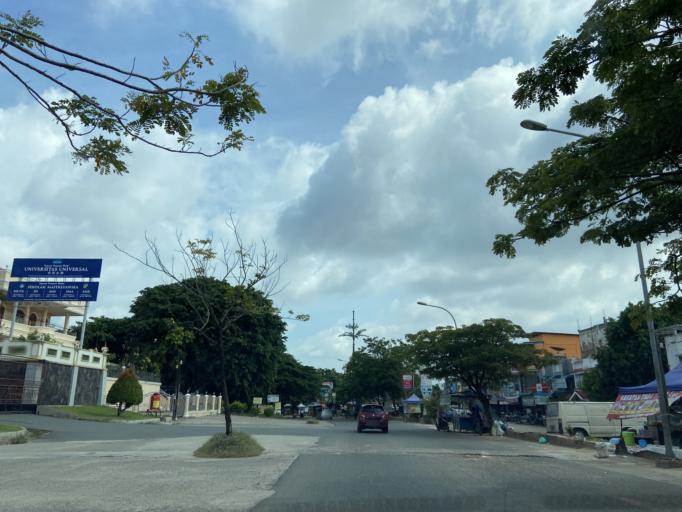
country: SG
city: Singapore
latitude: 1.1300
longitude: 104.0351
